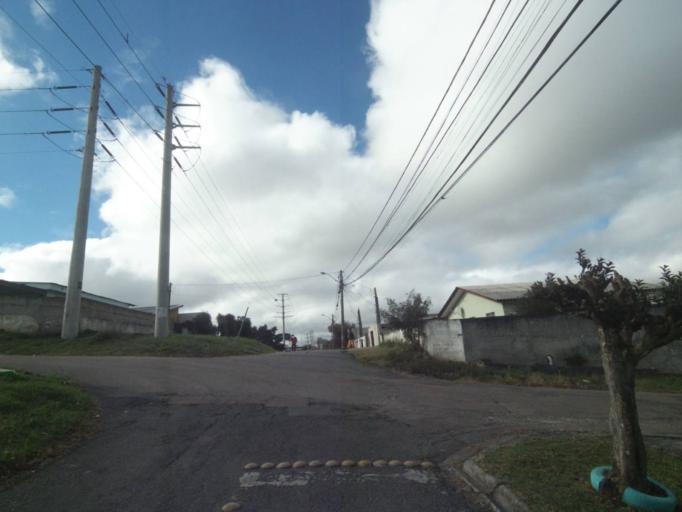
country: BR
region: Parana
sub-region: Sao Jose Dos Pinhais
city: Sao Jose dos Pinhais
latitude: -25.5209
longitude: -49.3055
